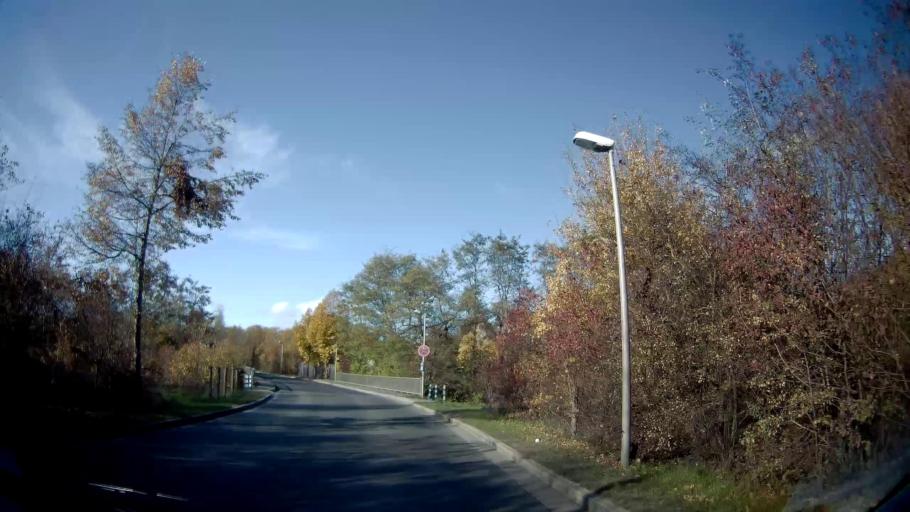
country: DE
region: North Rhine-Westphalia
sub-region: Regierungsbezirk Munster
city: Gladbeck
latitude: 51.5540
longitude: 6.9969
